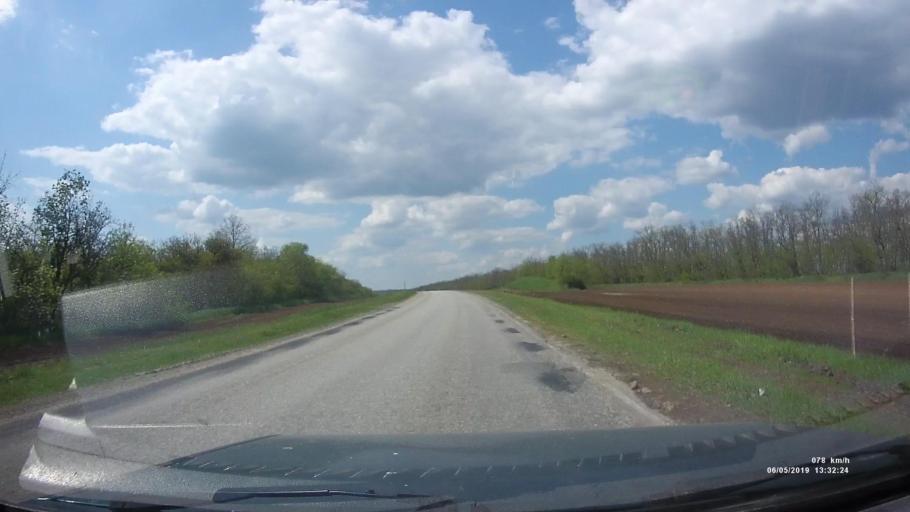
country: RU
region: Rostov
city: Ust'-Donetskiy
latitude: 47.6830
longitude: 40.7966
